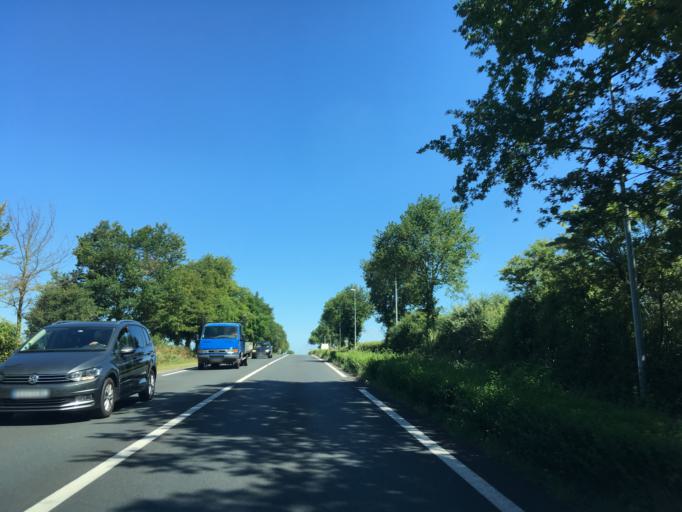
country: FR
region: Pays de la Loire
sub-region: Departement de la Vendee
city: Saint-Georges-de-Montaigu
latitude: 46.9535
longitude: -1.3045
